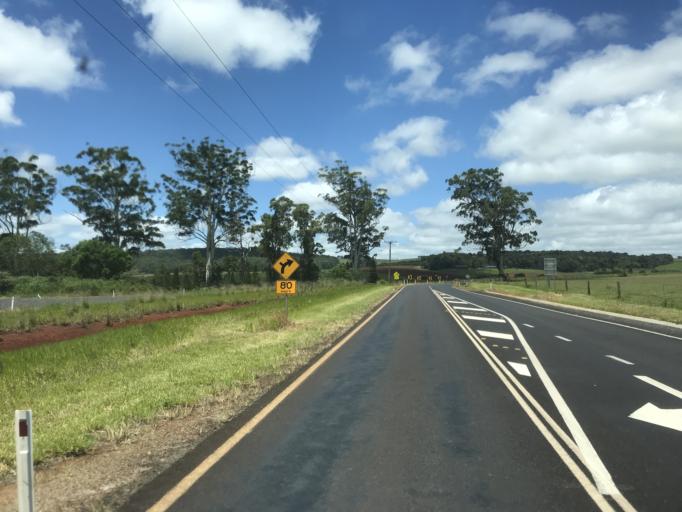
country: AU
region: Queensland
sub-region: Tablelands
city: Ravenshoe
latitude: -17.5089
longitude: 145.4557
